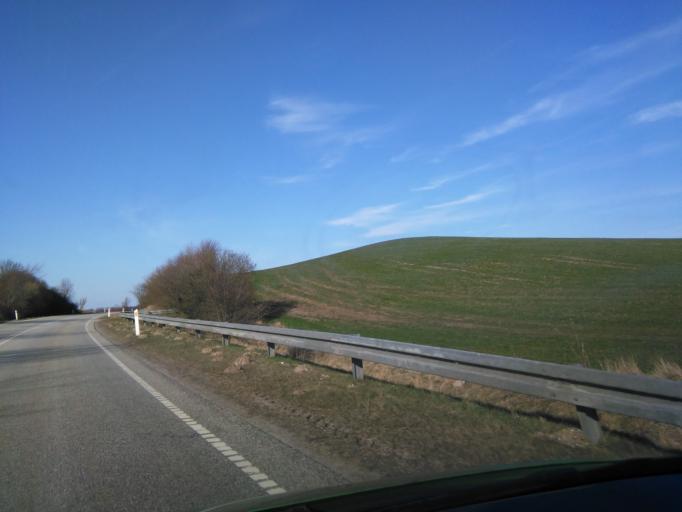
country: DK
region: Central Jutland
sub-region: Horsens Kommune
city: Braedstrup
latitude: 55.9298
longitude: 9.6794
